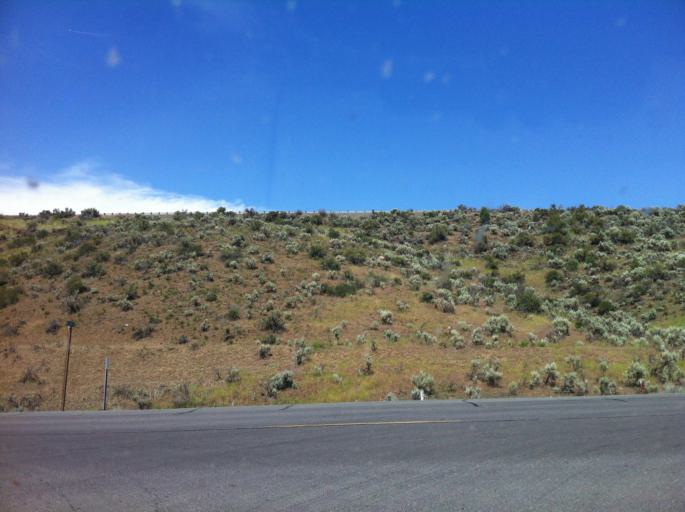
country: US
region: Oregon
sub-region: Baker County
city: Baker City
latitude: 44.7201
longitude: -117.7749
